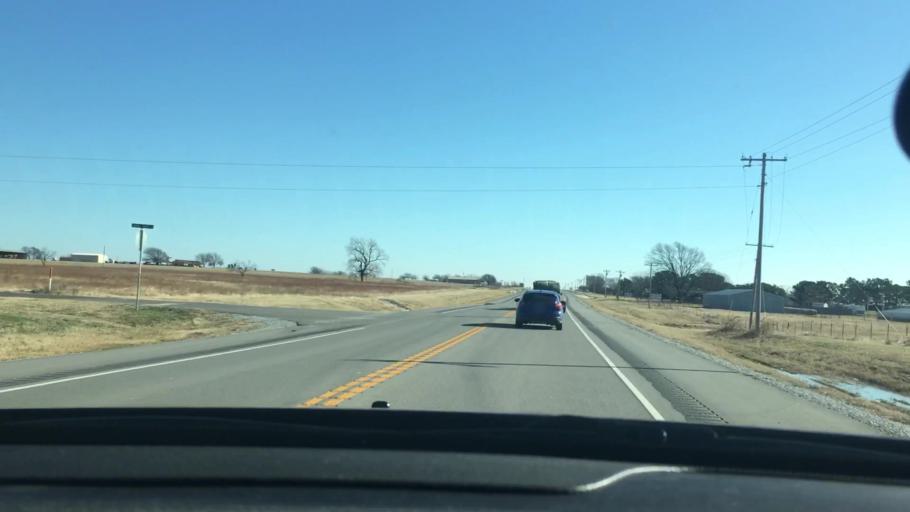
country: US
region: Oklahoma
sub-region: Love County
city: Marietta
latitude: 33.9404
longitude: -97.1644
